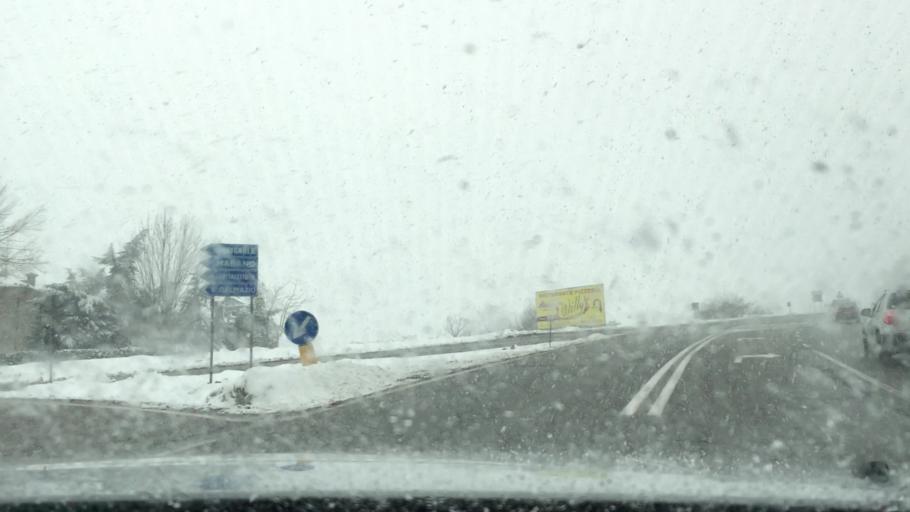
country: IT
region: Emilia-Romagna
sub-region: Provincia di Modena
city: Sant'Antonio
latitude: 44.4078
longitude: 10.8391
